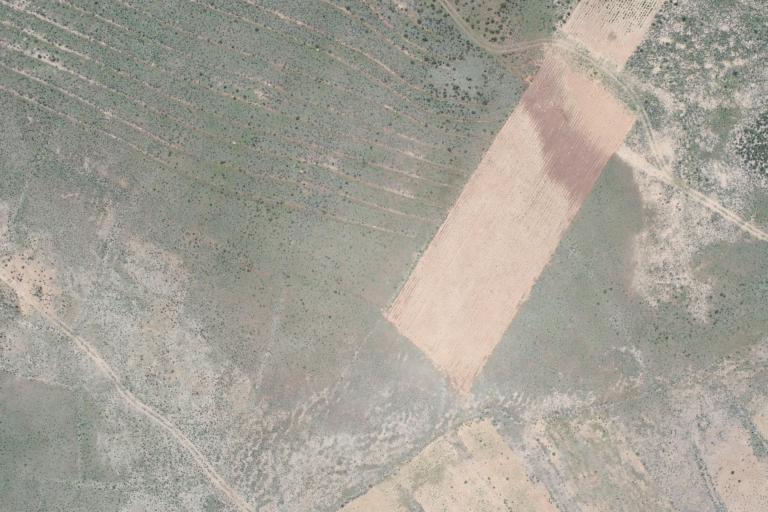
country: BO
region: La Paz
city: Curahuara de Carangas
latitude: -17.3110
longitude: -68.5203
